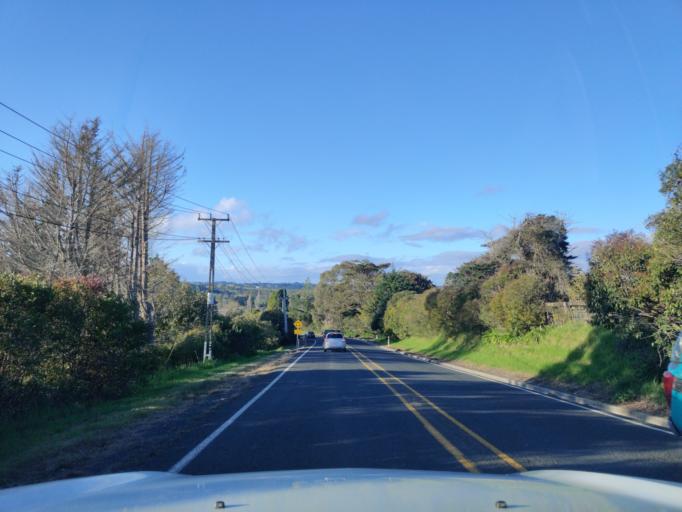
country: NZ
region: Auckland
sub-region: Auckland
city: Pakuranga
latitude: -36.9448
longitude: 174.9594
